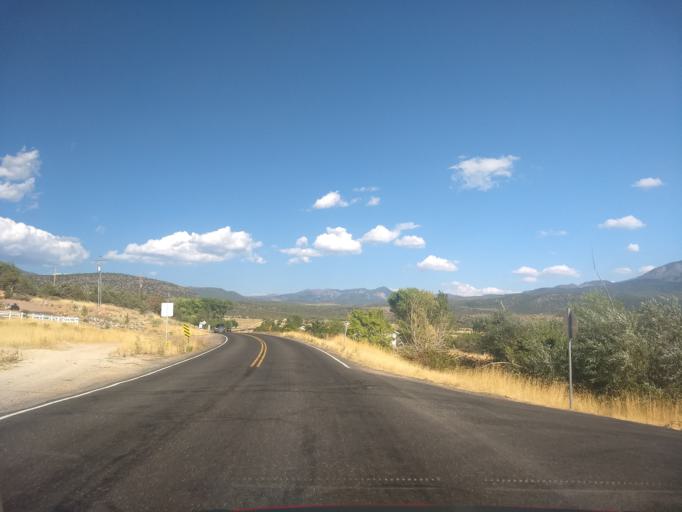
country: US
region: Utah
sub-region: Washington County
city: Enterprise
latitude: 37.4167
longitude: -113.6246
